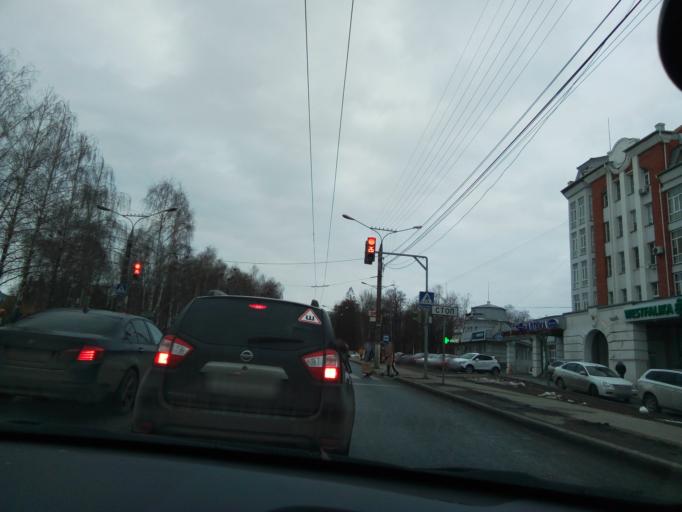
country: RU
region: Chuvashia
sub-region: Cheboksarskiy Rayon
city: Cheboksary
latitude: 56.1463
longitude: 47.2282
